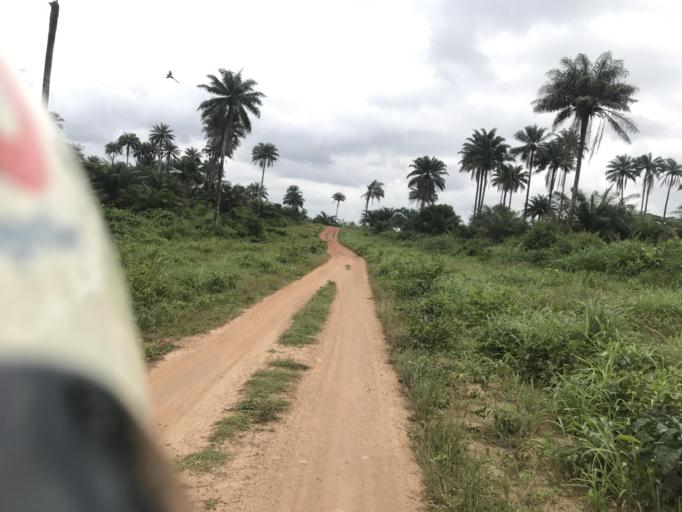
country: SL
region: Eastern Province
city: Kailahun
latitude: 8.3421
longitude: -10.4744
